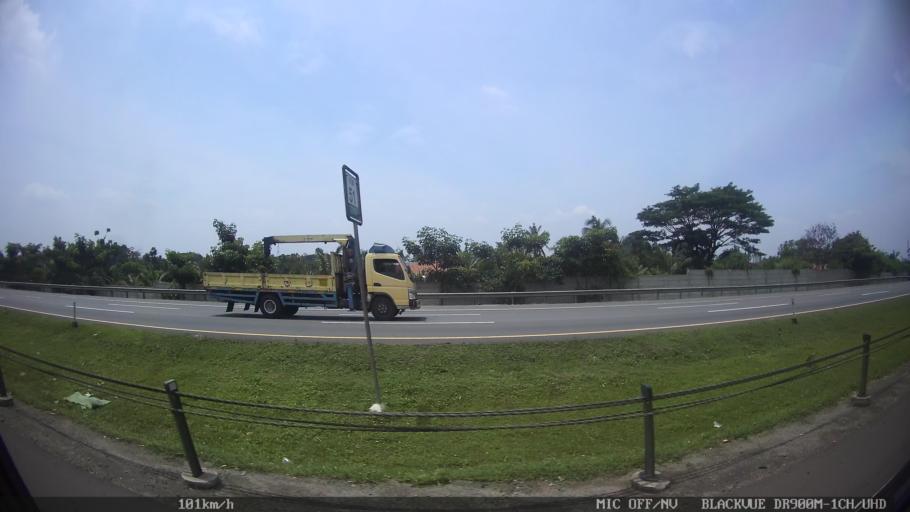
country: ID
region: West Java
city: Kresek
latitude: -6.1762
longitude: 106.3540
